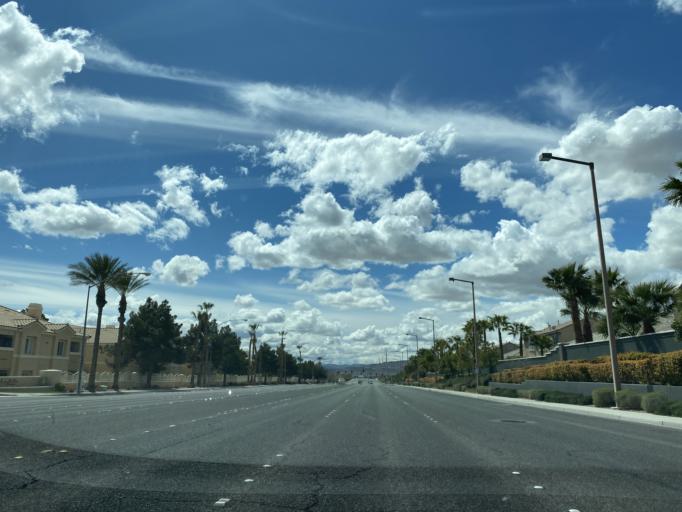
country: US
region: Nevada
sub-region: Clark County
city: Summerlin South
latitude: 36.1256
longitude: -115.3152
